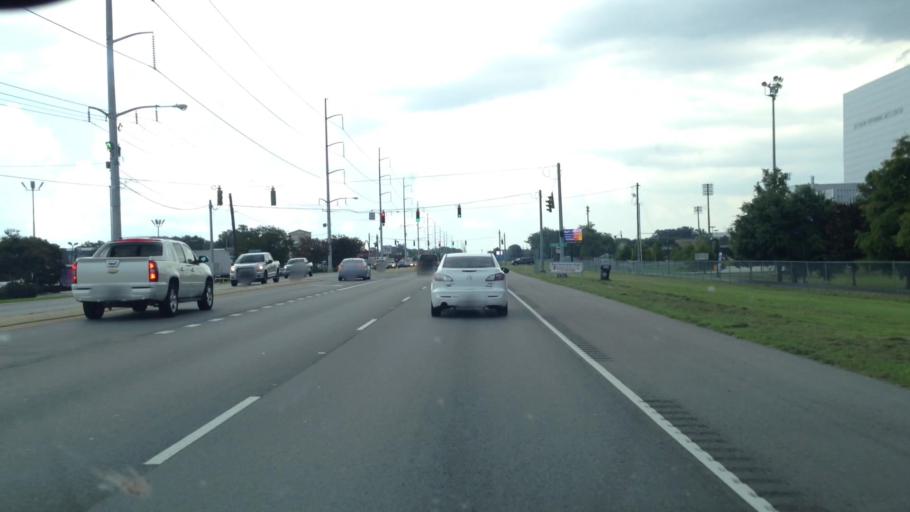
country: US
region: Louisiana
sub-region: Jefferson Parish
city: River Ridge
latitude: 29.9773
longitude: -90.2053
